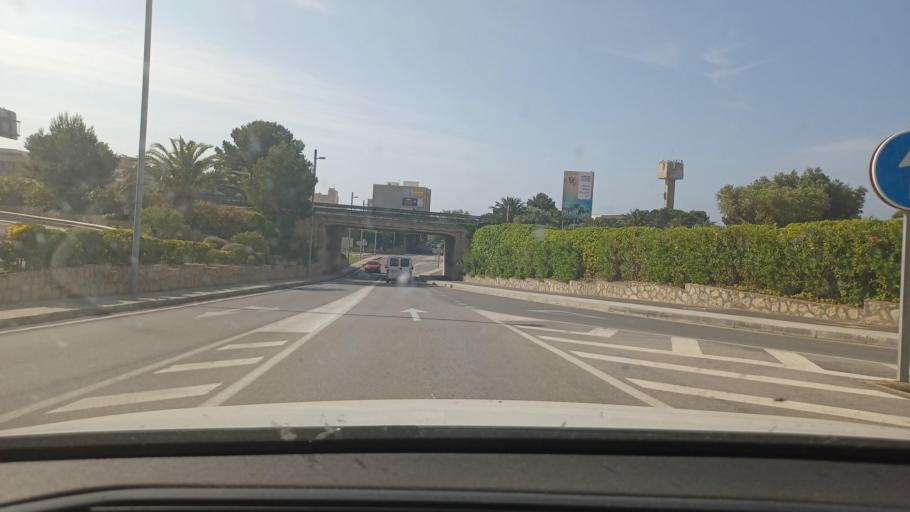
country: ES
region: Catalonia
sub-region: Provincia de Tarragona
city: Colldejou
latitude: 40.9972
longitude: 0.9187
